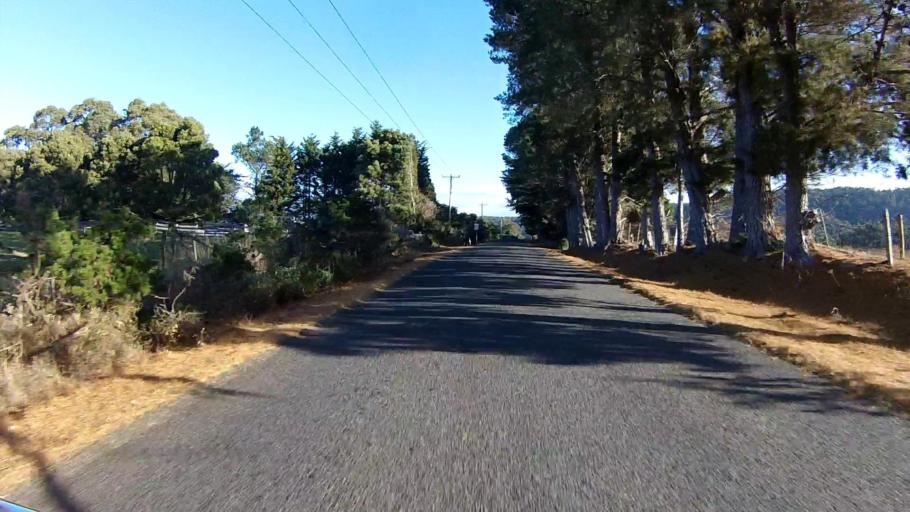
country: AU
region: Tasmania
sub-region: Clarence
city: Sandford
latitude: -43.1690
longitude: 147.8584
